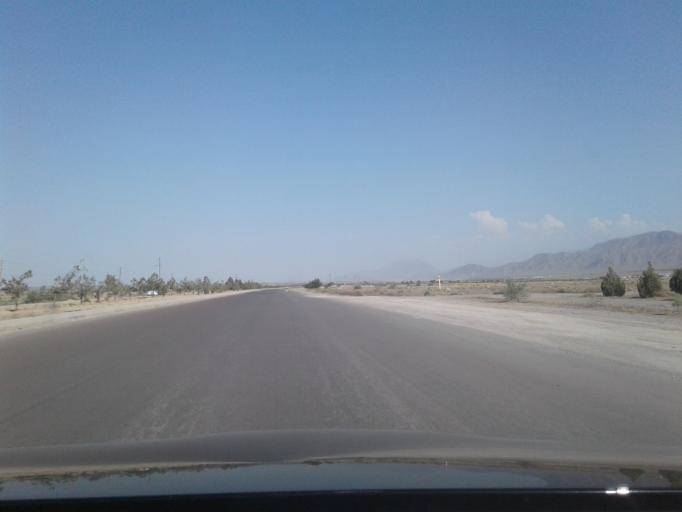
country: TM
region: Ahal
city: Baharly
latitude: 38.2291
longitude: 57.7881
